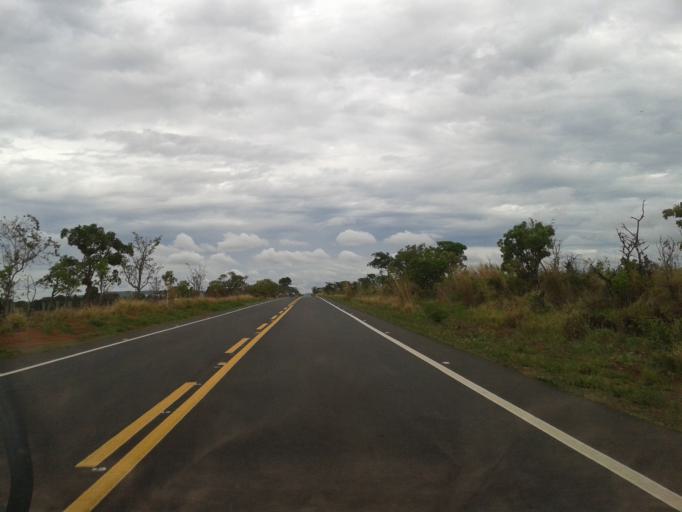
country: BR
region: Goias
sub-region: Caldas Novas
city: Caldas Novas
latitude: -17.8859
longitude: -48.6513
